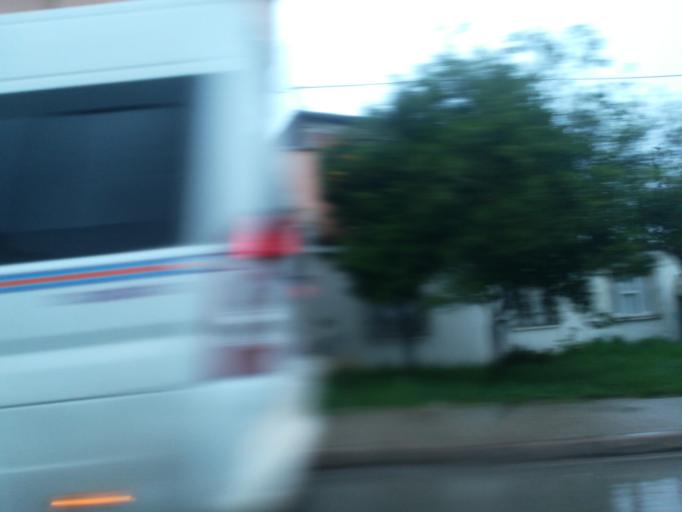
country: TR
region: Adana
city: Seyhan
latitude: 36.9973
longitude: 35.2806
